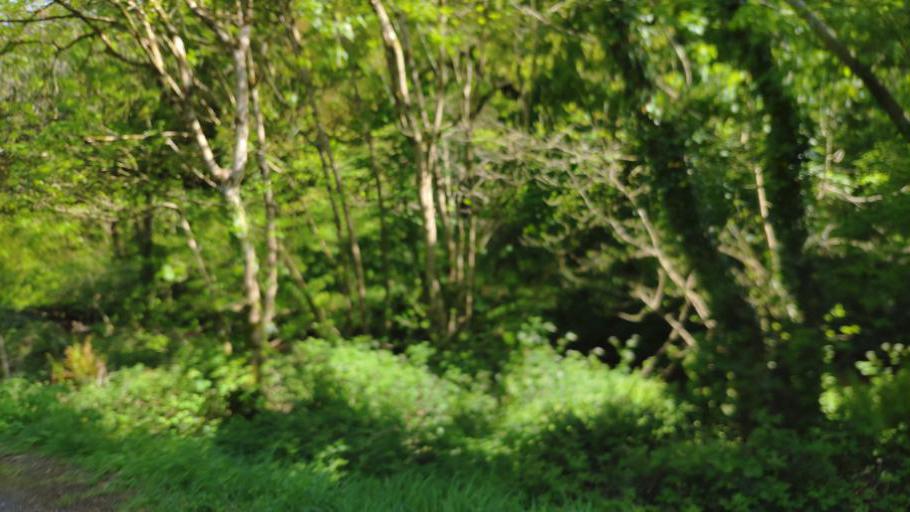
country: IE
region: Munster
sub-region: County Cork
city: Blarney
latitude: 51.9427
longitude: -8.5653
